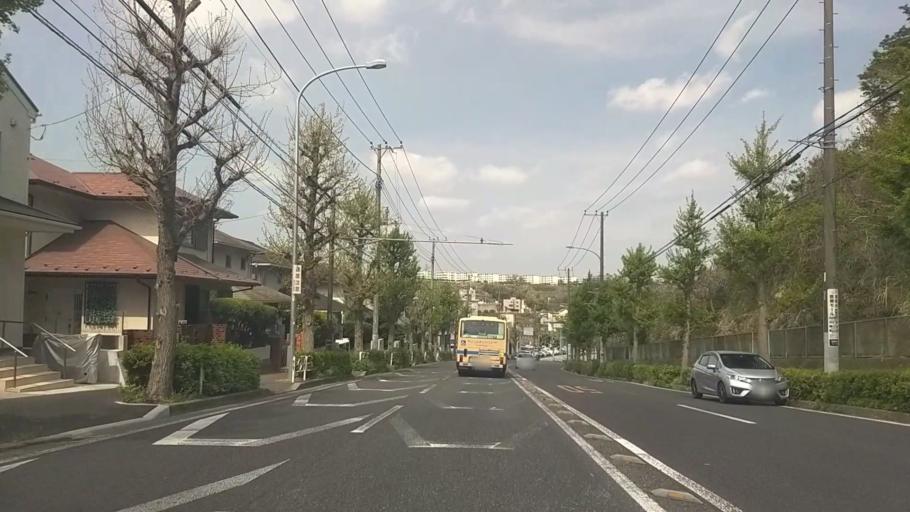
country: JP
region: Kanagawa
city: Yokohama
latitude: 35.3880
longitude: 139.5859
